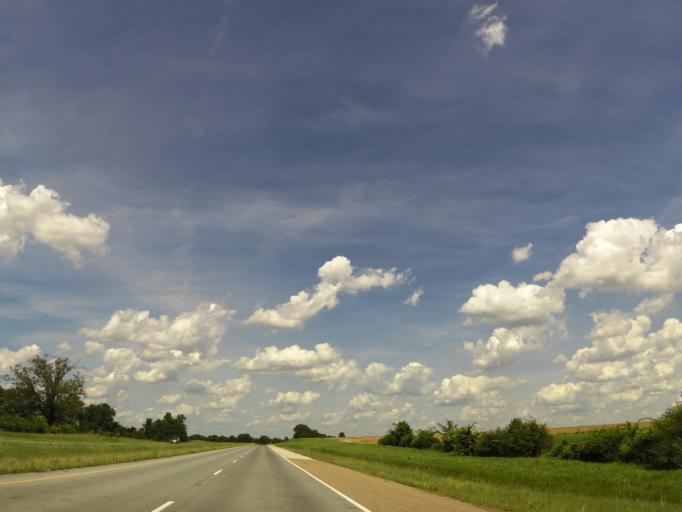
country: US
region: Tennessee
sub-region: Gibson County
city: Dyer
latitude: 35.9924
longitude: -89.0353
